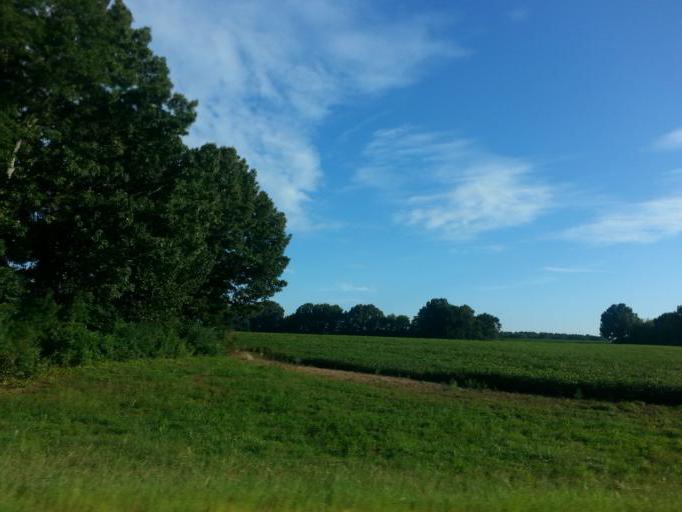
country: US
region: Alabama
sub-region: Lauderdale County
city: Killen
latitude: 34.8609
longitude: -87.4646
